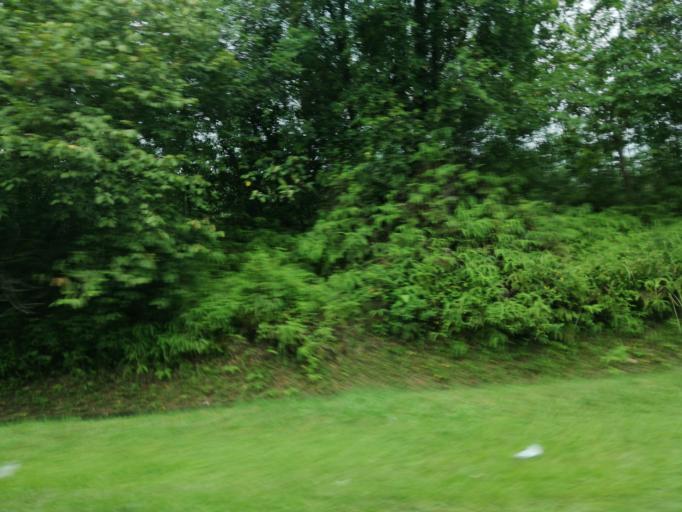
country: MY
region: Penang
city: Tasek Glugor
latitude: 5.4972
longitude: 100.6102
